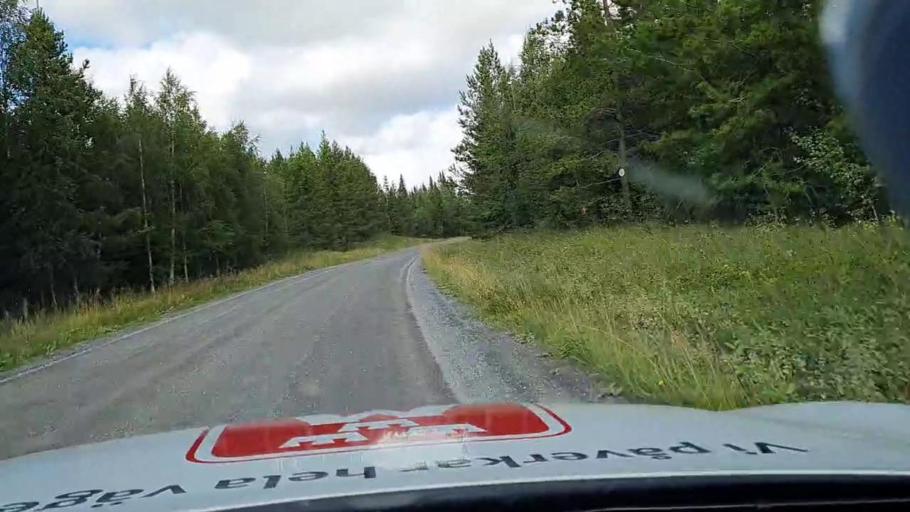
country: SE
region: Jaemtland
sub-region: Stroemsunds Kommun
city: Stroemsund
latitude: 63.7548
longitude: 15.2310
